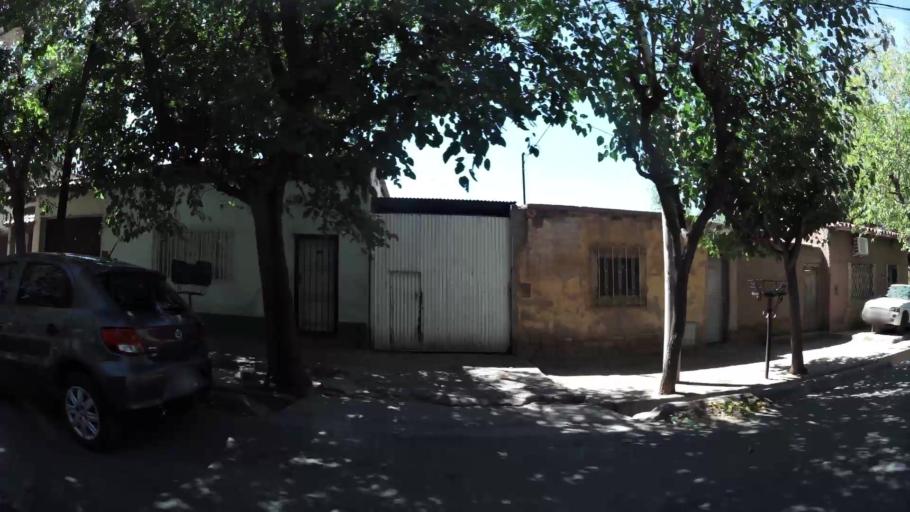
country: AR
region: Mendoza
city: Mendoza
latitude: -32.8802
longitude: -68.8043
